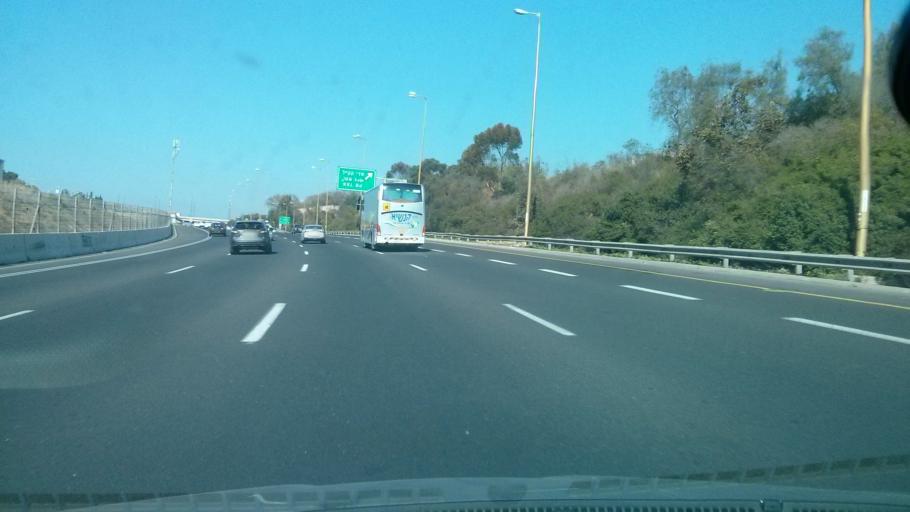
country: IL
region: Tel Aviv
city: Ramat Gan
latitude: 32.1139
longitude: 34.8111
